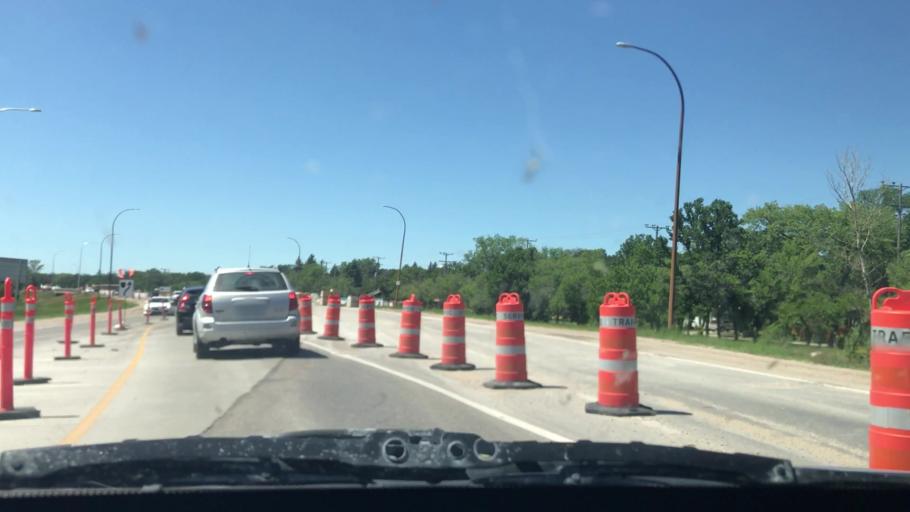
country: CA
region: Manitoba
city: Winnipeg
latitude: 49.8576
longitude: -97.0910
